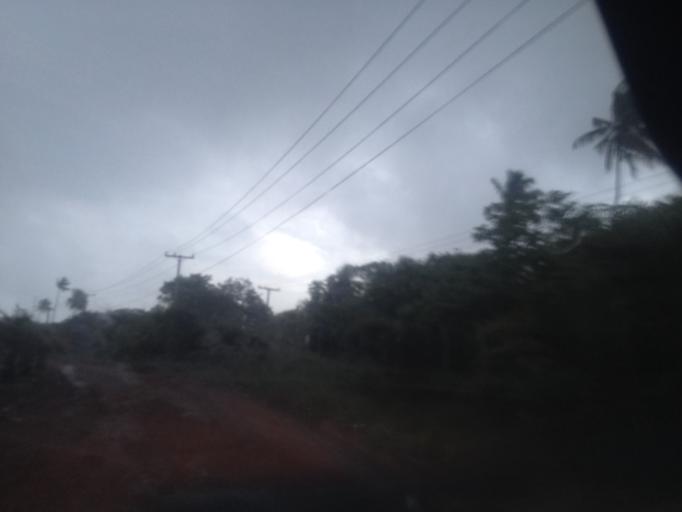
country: BR
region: Bahia
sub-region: Mata De Sao Joao
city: Mata de Sao Joao
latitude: -12.5746
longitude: -38.0288
